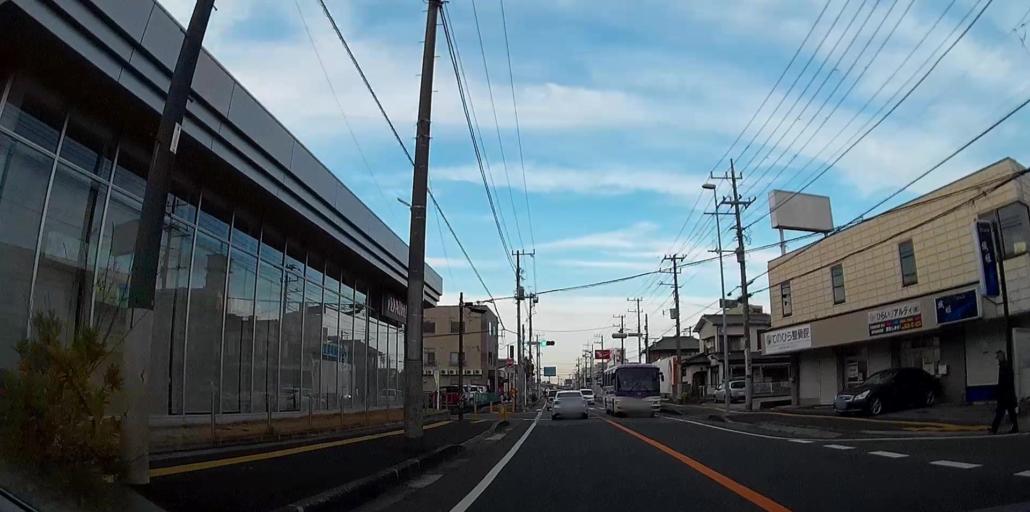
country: JP
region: Chiba
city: Ichihara
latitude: 35.4765
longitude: 140.0446
